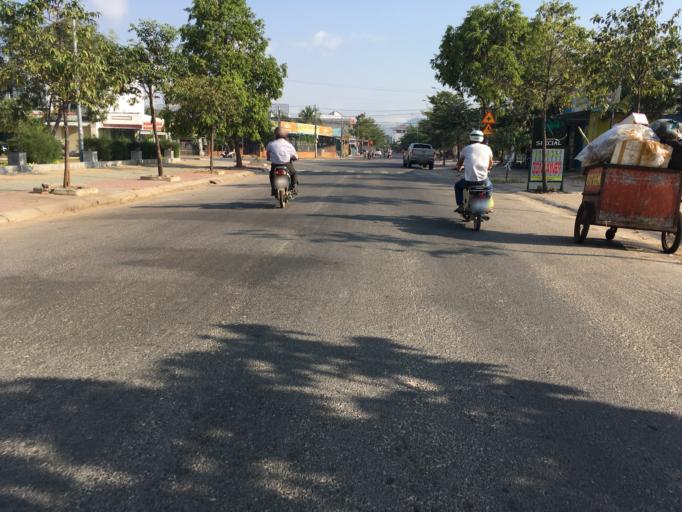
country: VN
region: Ninh Thuan
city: Phan Rang-Thap Cham
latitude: 11.5669
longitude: 108.9984
